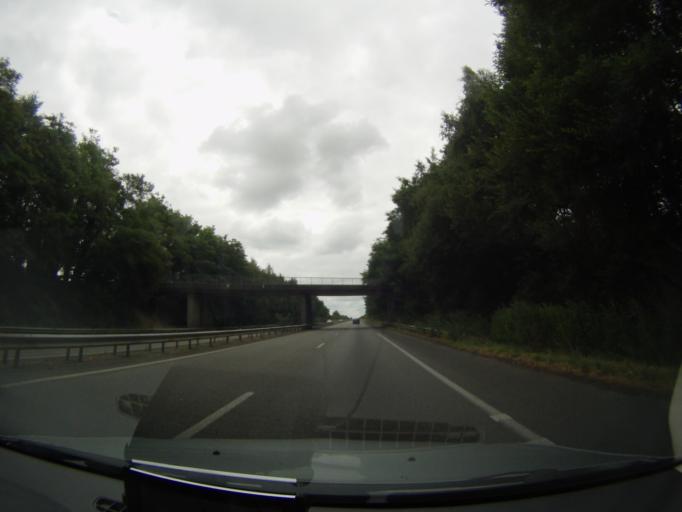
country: FR
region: Pays de la Loire
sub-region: Departement de la Loire-Atlantique
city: Treillieres
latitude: 47.3544
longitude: -1.6562
